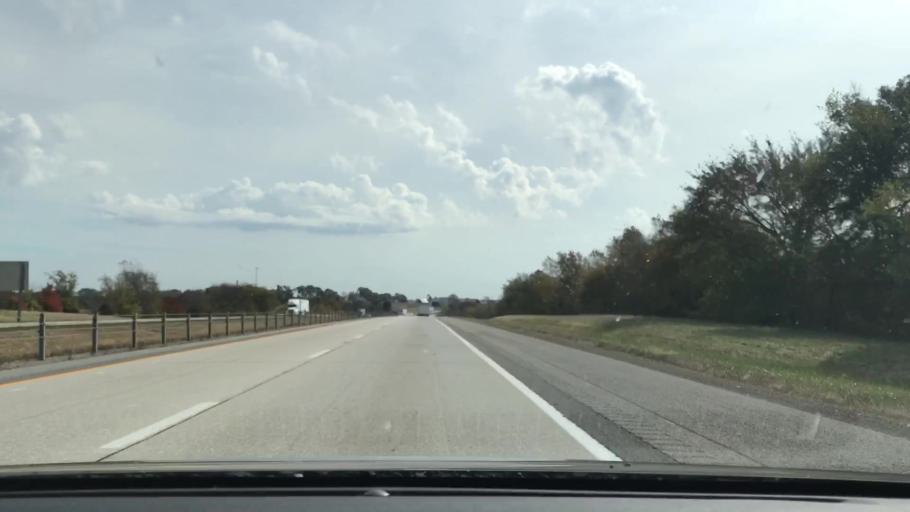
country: US
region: Kentucky
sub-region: Trigg County
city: Cadiz
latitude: 36.8739
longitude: -87.7216
